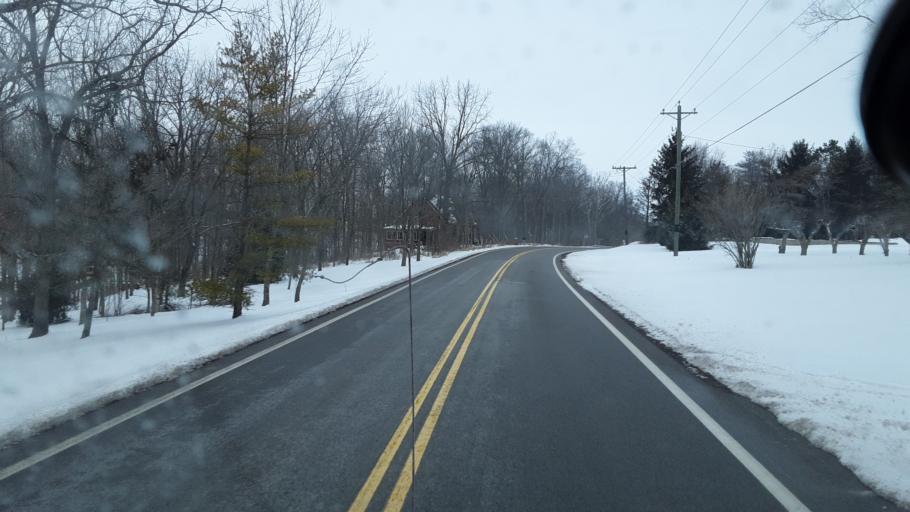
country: US
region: Ohio
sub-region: Madison County
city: Plain City
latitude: 40.1498
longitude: -83.3452
